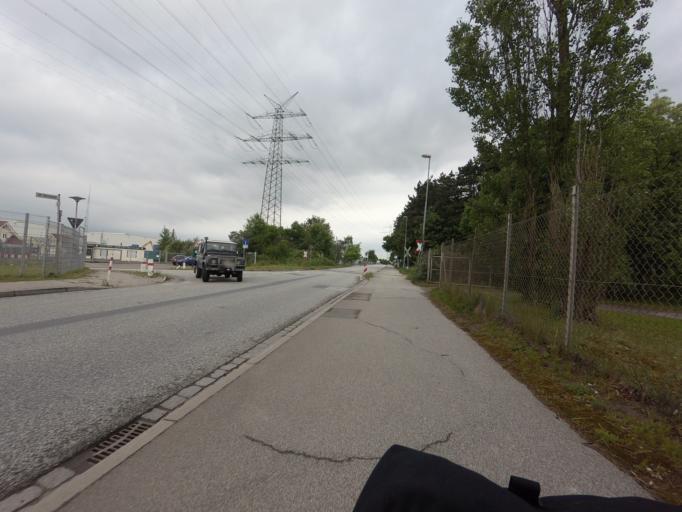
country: DE
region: Mecklenburg-Vorpommern
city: Selmsdorf
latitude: 53.8985
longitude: 10.7975
